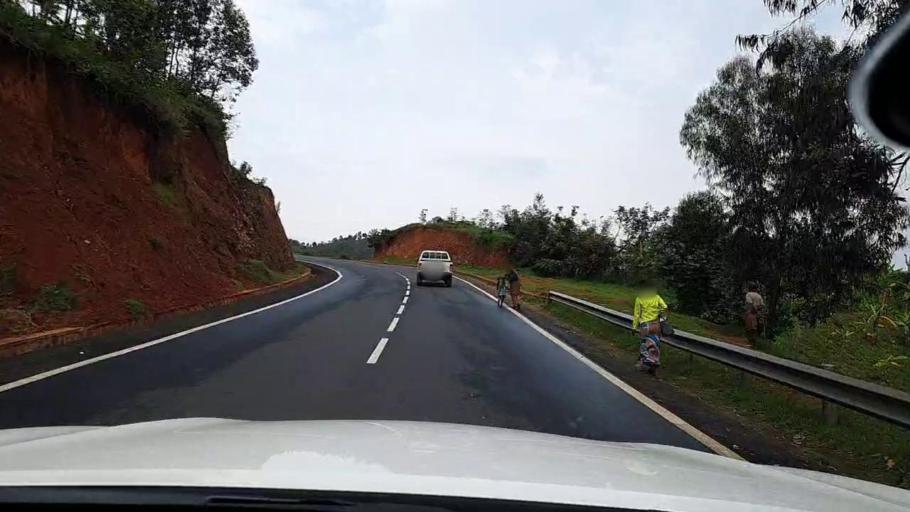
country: RW
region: Western Province
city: Kibuye
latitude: -2.1653
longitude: 29.2932
